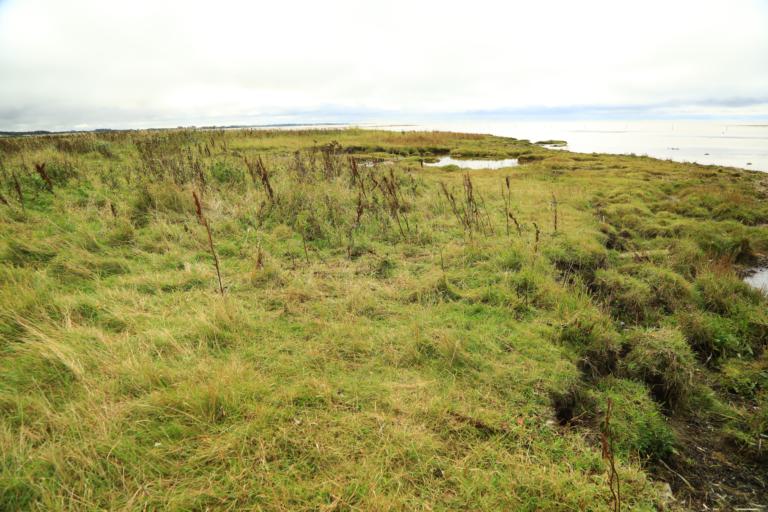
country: SE
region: Halland
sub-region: Varbergs Kommun
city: Tvaaker
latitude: 57.0171
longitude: 12.3372
